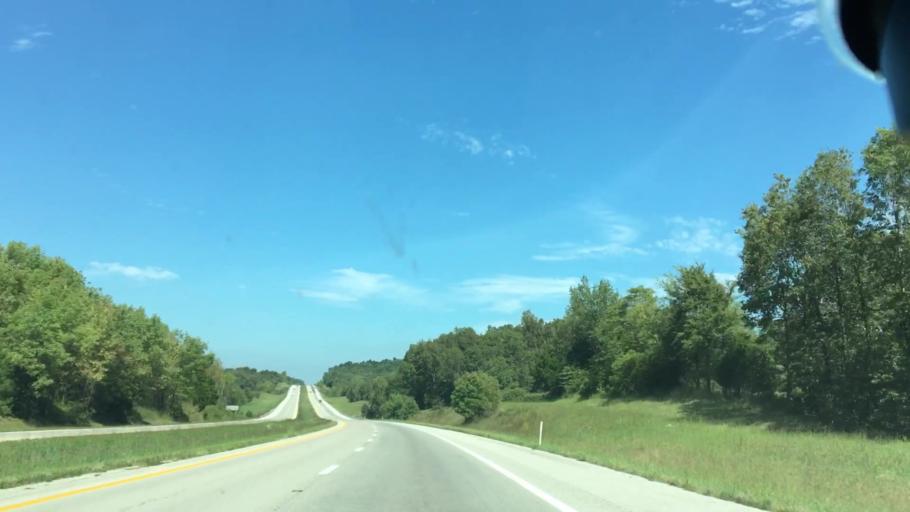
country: US
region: Kentucky
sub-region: Christian County
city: Hopkinsville
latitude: 36.9300
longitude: -87.4703
